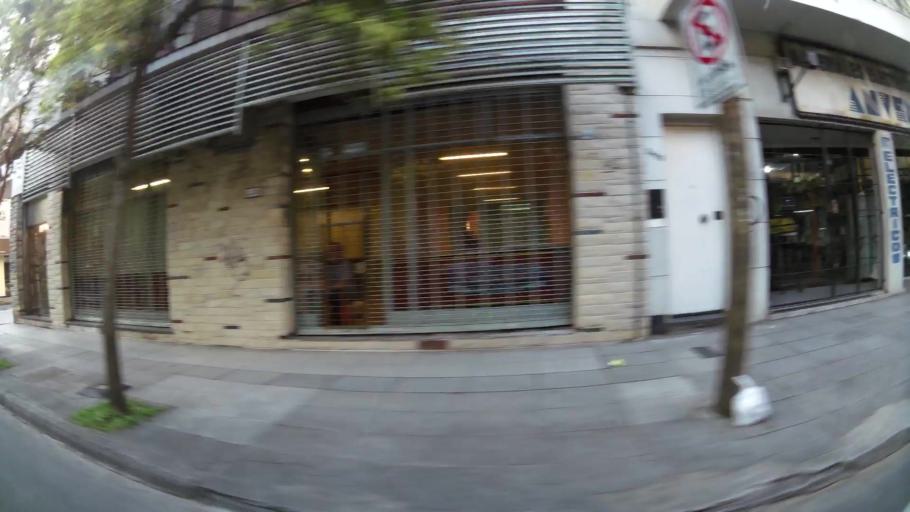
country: AR
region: Buenos Aires
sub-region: Partido de Vicente Lopez
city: Olivos
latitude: -34.5355
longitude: -58.5076
